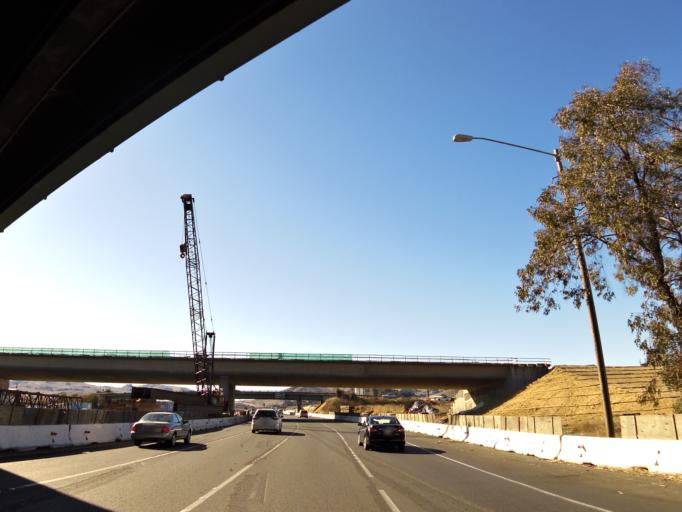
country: US
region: California
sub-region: Solano County
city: Green Valley
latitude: 38.2169
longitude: -122.1379
